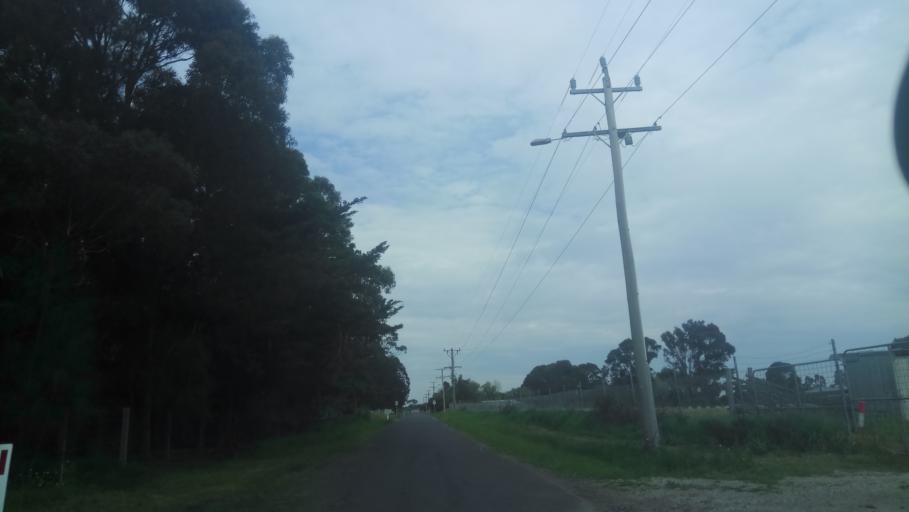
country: AU
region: Victoria
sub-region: Kingston
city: Chelsea Heights
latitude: -38.0277
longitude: 145.1382
